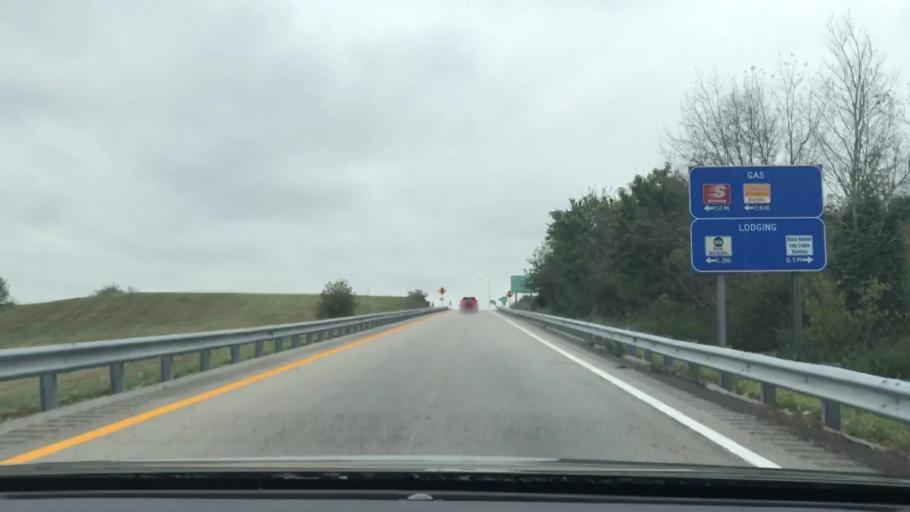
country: US
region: Kentucky
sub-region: Adair County
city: Columbia
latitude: 37.0869
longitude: -85.3053
